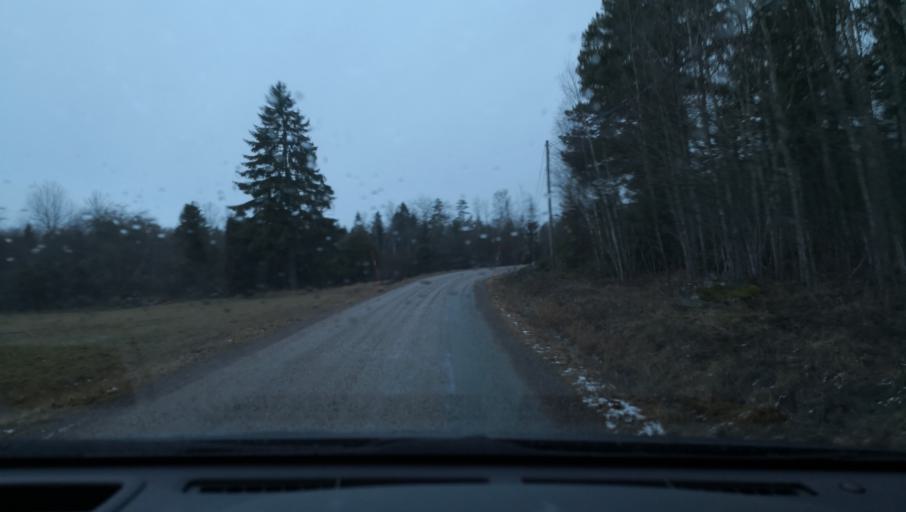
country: SE
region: Uppsala
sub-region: Enkopings Kommun
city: Hummelsta
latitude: 59.4583
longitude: 16.8468
